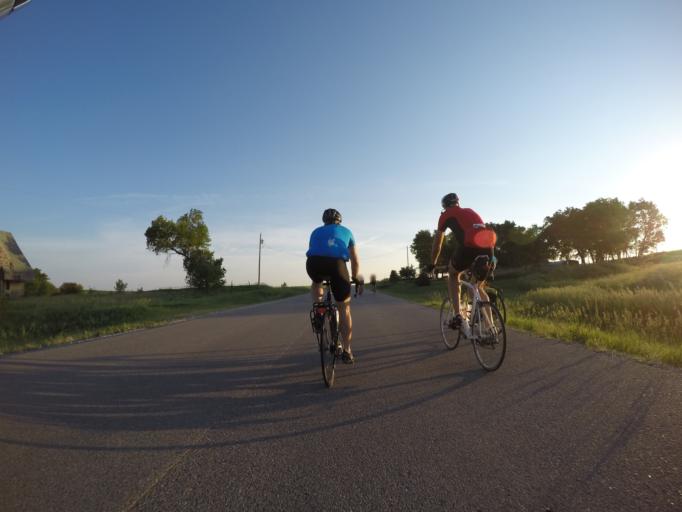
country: US
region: Kansas
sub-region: Marshall County
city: Marysville
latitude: 39.8487
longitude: -96.6009
